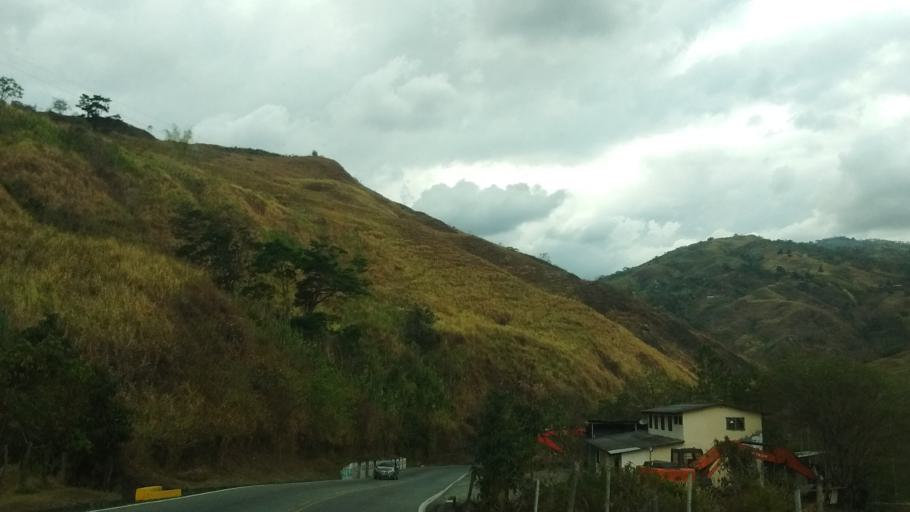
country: CO
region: Cauca
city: Rosas
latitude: 2.2785
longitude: -76.7080
